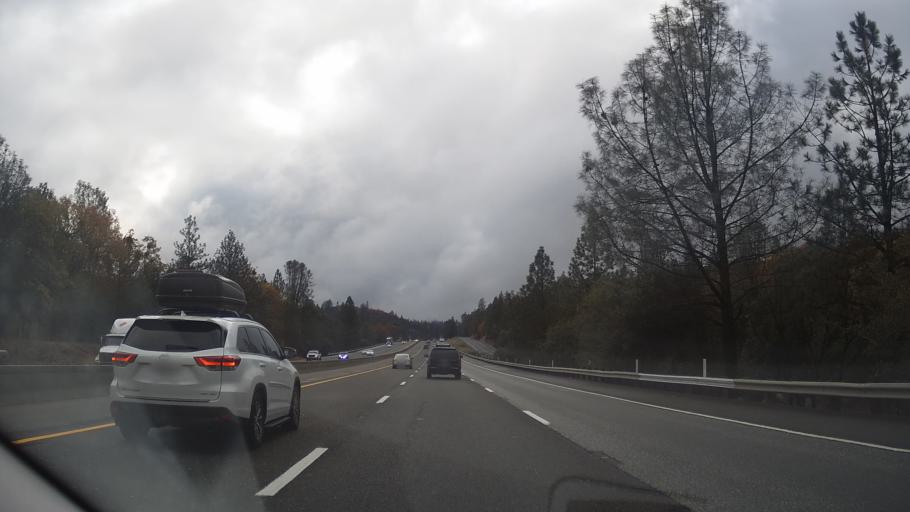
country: US
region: California
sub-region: Placer County
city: Meadow Vista
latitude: 38.9810
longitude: -121.0094
